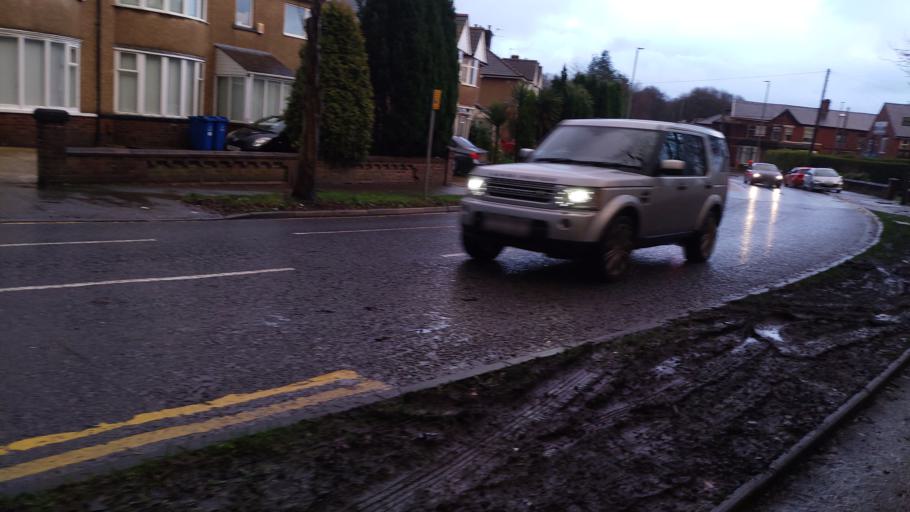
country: GB
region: England
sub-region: Blackburn with Darwen
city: Blackburn
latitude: 53.7413
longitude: -2.5083
